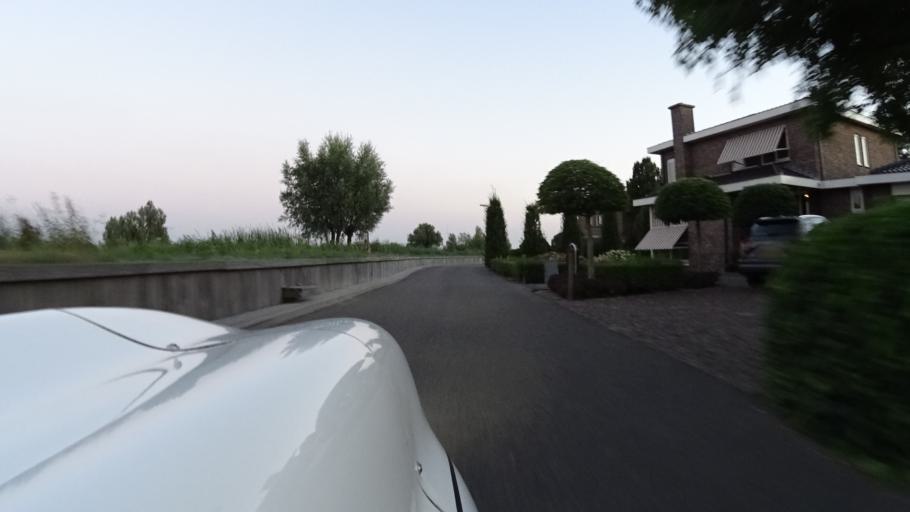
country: NL
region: South Holland
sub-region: Gemeente Kaag en Braassem
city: Oude Wetering
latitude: 52.1810
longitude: 4.6308
